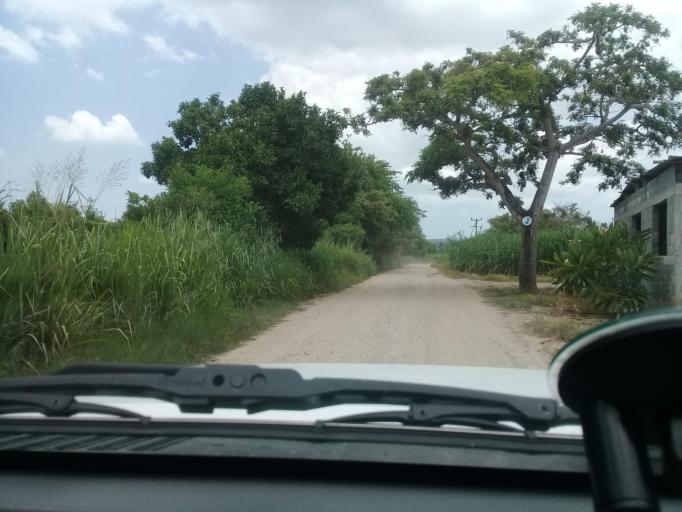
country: MX
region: Veracruz
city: Panuco
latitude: 22.1301
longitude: -98.0644
